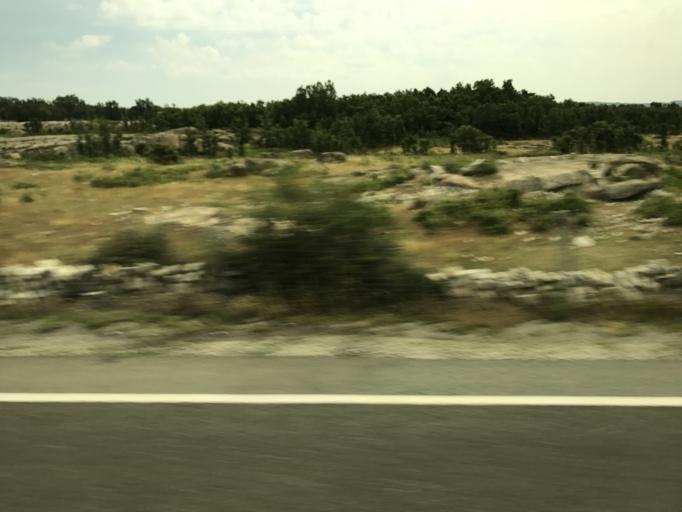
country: ES
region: Madrid
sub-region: Provincia de Madrid
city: La Cabrera
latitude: 40.9114
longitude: -3.6090
